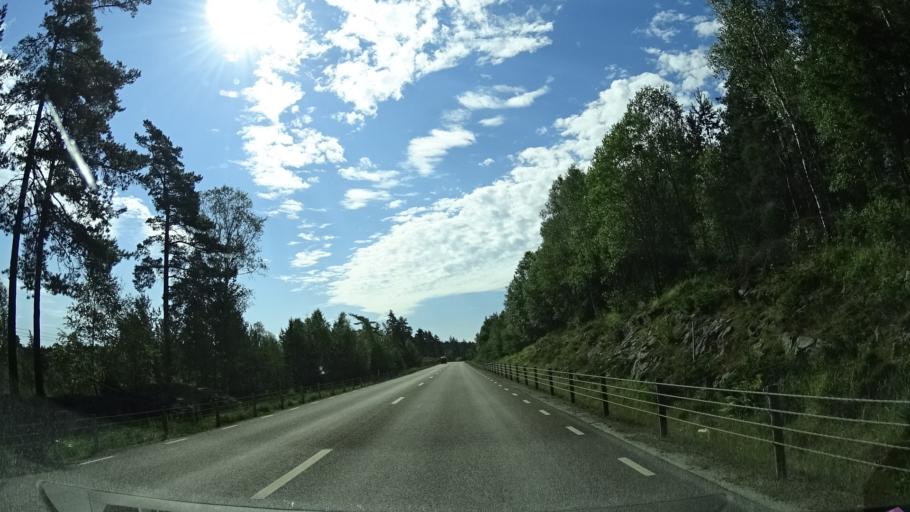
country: SE
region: Vaermland
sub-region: Arjangs Kommun
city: Arjaeng
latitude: 59.4380
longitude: 12.0892
